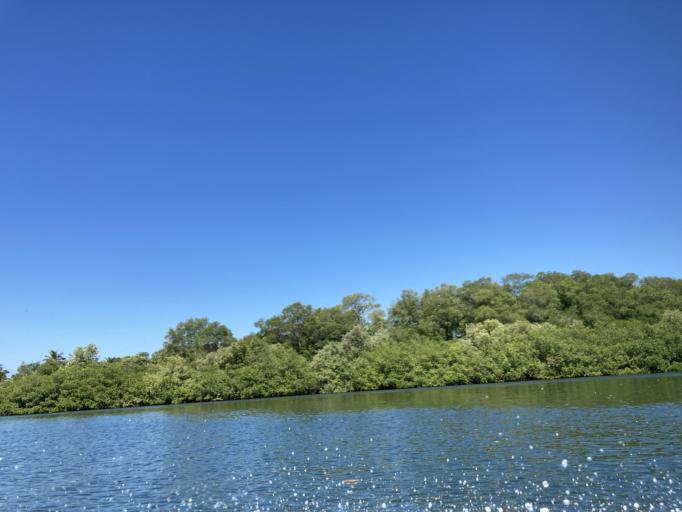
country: GT
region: Jutiapa
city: Pasaco
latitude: 13.8042
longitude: -90.2655
